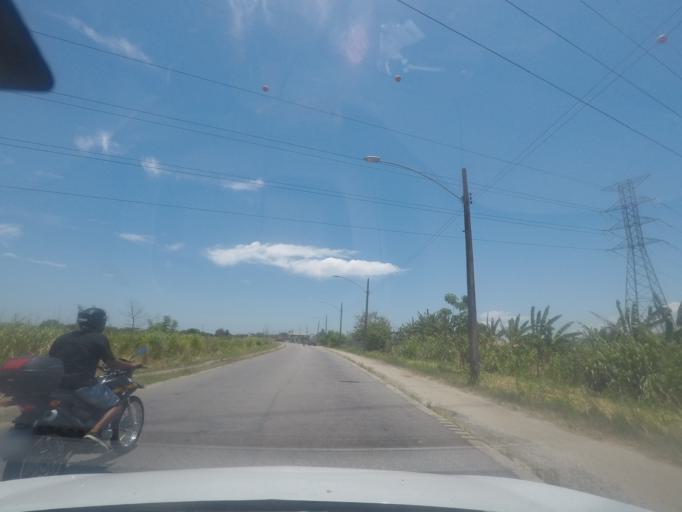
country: BR
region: Rio de Janeiro
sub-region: Itaguai
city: Itaguai
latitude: -22.8981
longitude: -43.6879
